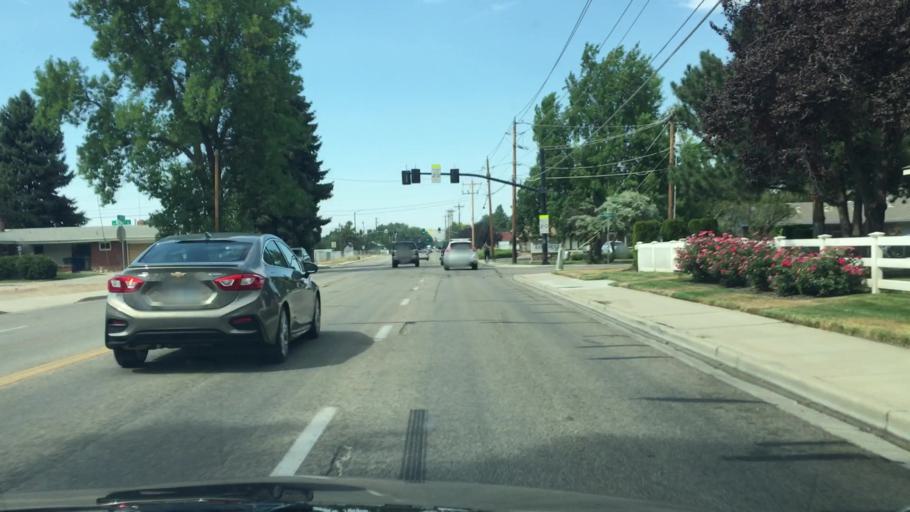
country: US
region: Idaho
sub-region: Ada County
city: Garden City
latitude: 43.6231
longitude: -116.2742
